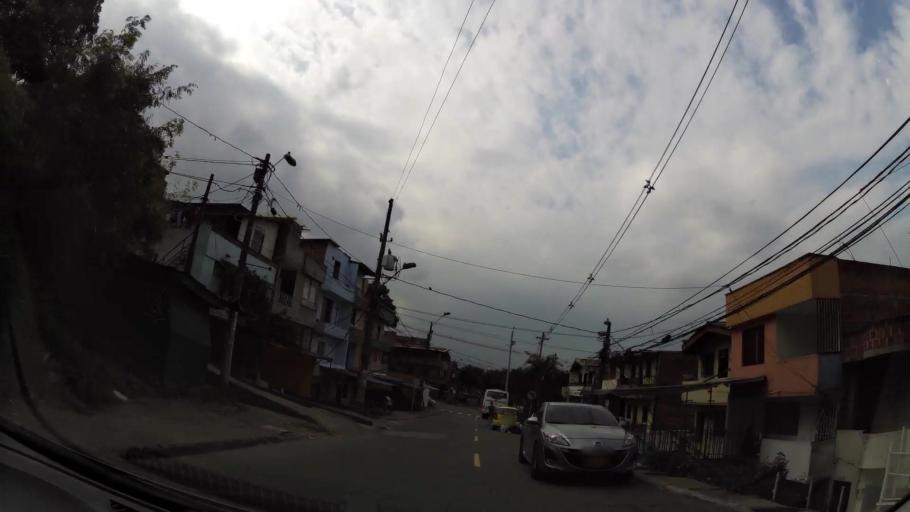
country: CO
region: Antioquia
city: Medellin
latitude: 6.2848
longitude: -75.5527
